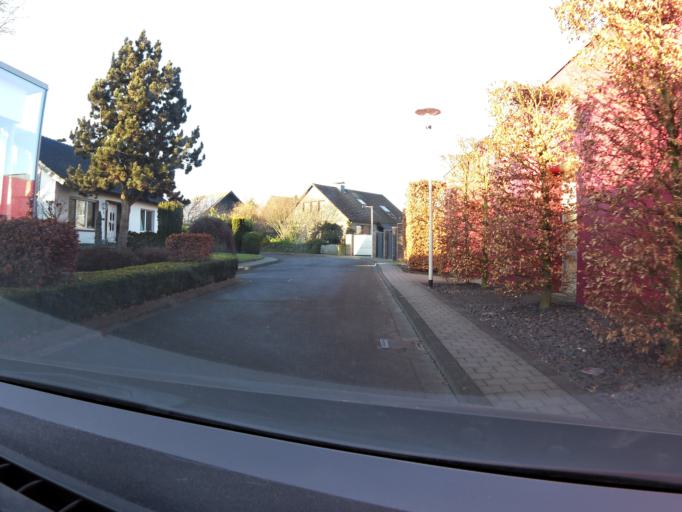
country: DE
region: North Rhine-Westphalia
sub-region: Regierungsbezirk Dusseldorf
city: Nettetal
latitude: 51.3373
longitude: 6.2321
